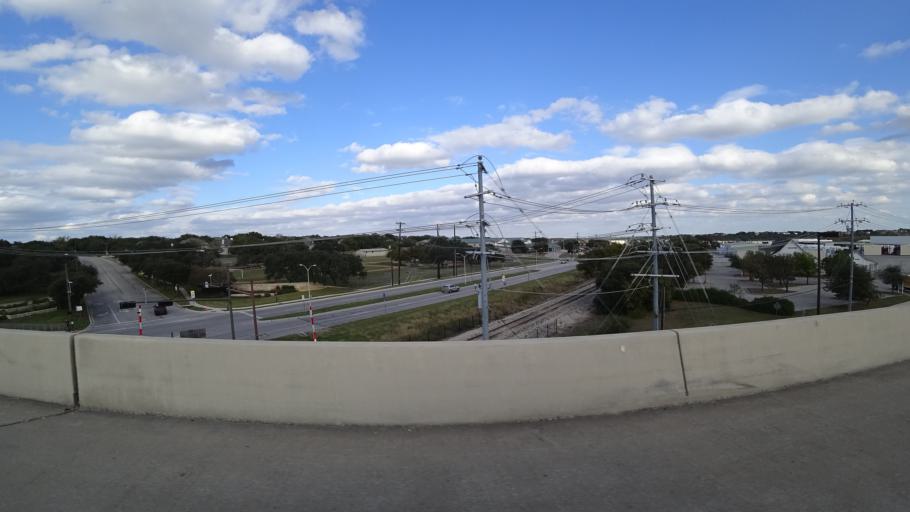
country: US
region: Texas
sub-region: Williamson County
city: Cedar Park
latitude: 30.5026
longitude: -97.8081
